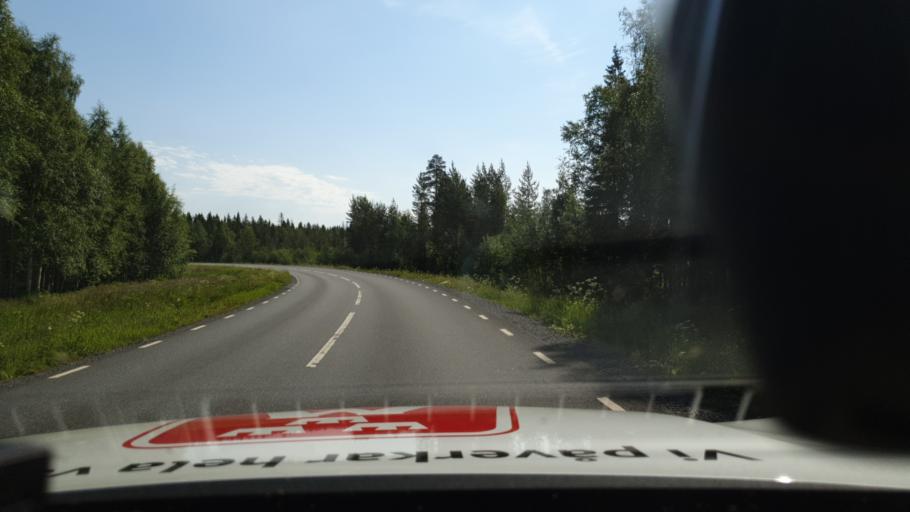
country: SE
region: Norrbotten
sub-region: Lulea Kommun
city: Gammelstad
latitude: 65.7868
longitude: 22.1016
